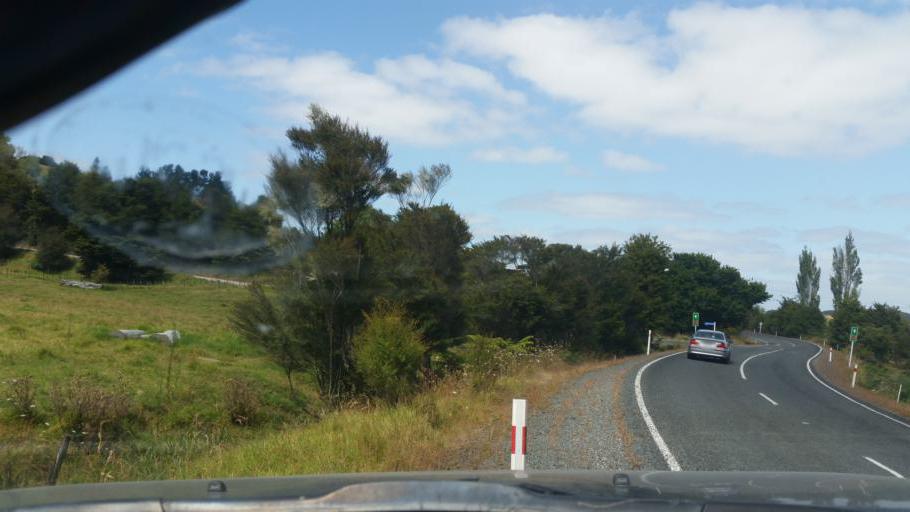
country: NZ
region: Northland
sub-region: Whangarei
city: Ruakaka
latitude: -35.9419
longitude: 174.2928
